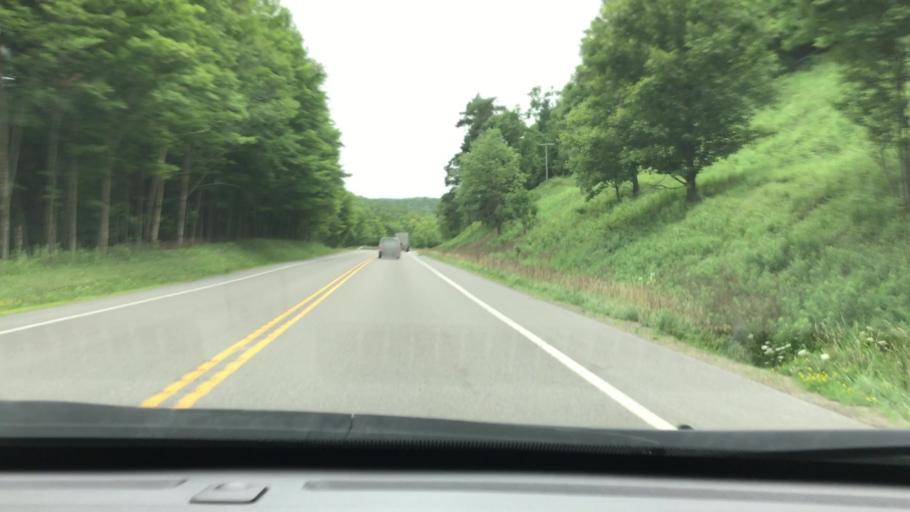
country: US
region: Pennsylvania
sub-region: McKean County
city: Kane
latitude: 41.6744
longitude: -78.6830
